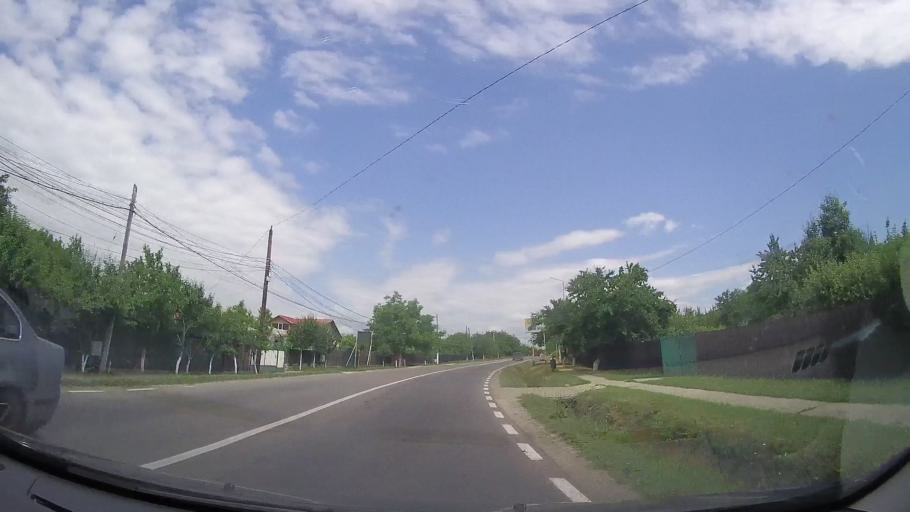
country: RO
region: Prahova
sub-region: Comuna Magurele
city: Magurele
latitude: 45.1148
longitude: 26.0342
